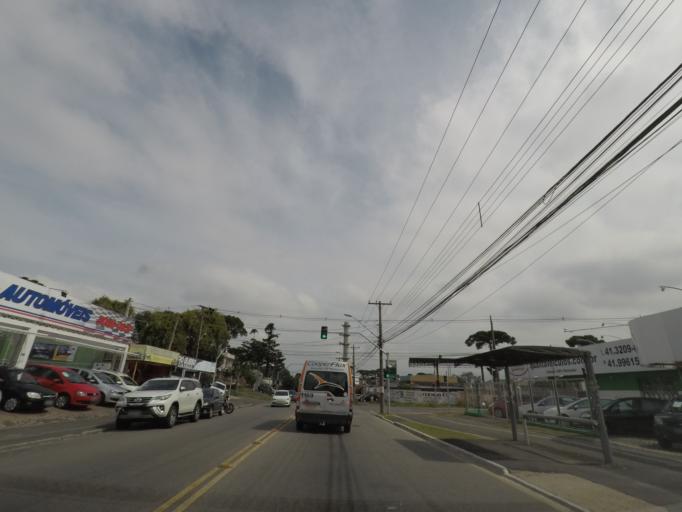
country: BR
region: Parana
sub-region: Curitiba
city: Curitiba
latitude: -25.4970
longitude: -49.2977
